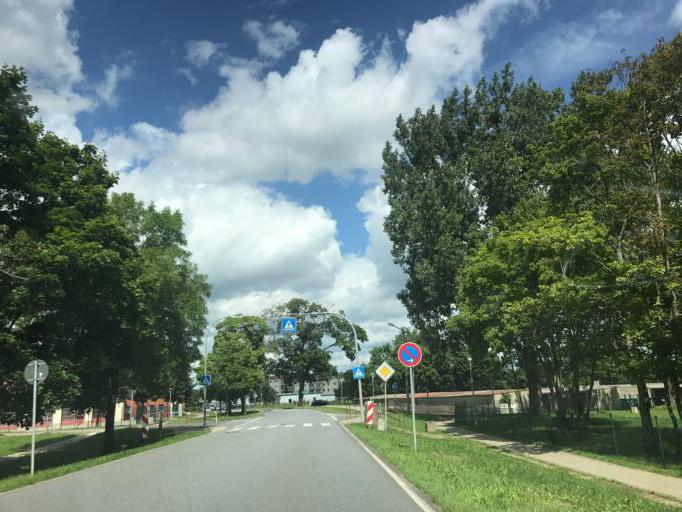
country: DE
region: Brandenburg
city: Gransee
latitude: 53.0008
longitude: 13.1541
